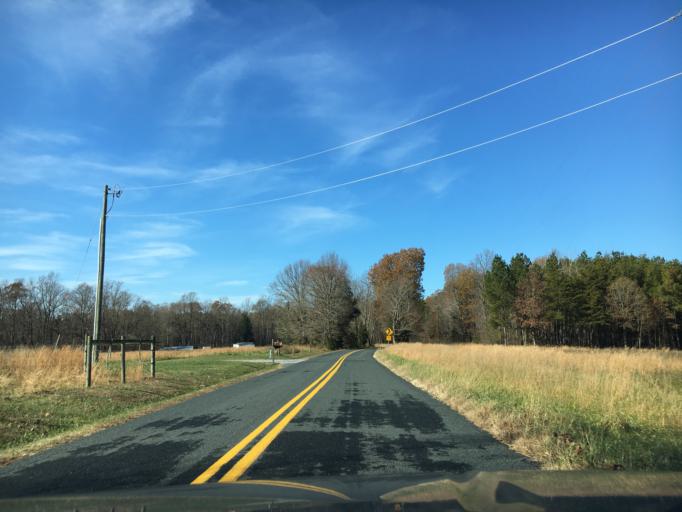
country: US
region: Virginia
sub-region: Buckingham County
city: Buckingham
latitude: 37.4342
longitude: -78.6279
